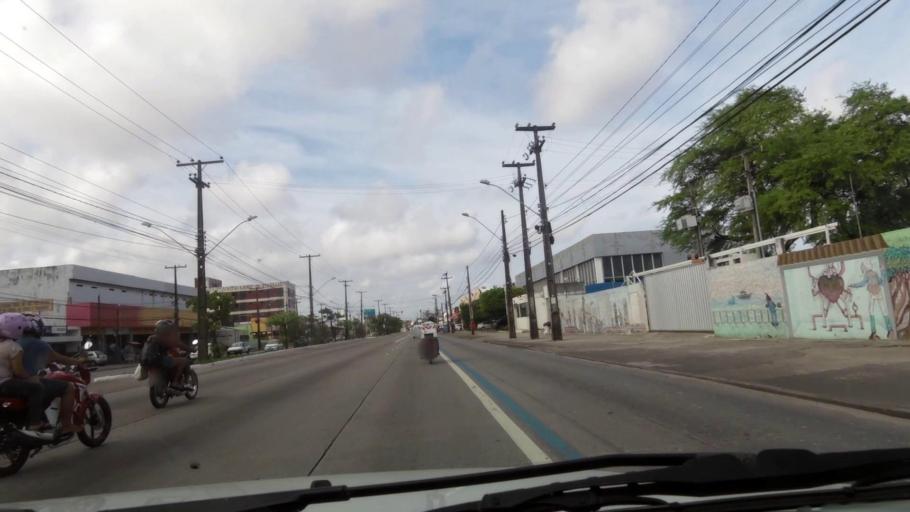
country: BR
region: Pernambuco
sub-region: Recife
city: Recife
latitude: -8.0854
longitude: -34.9072
